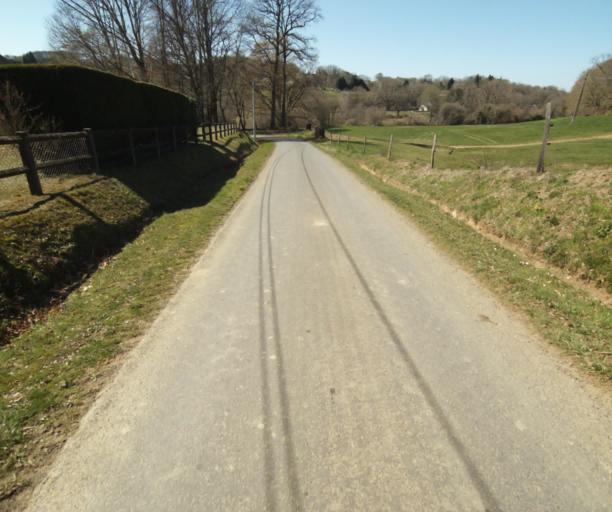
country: FR
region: Limousin
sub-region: Departement de la Correze
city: Chamboulive
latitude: 45.3969
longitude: 1.6517
